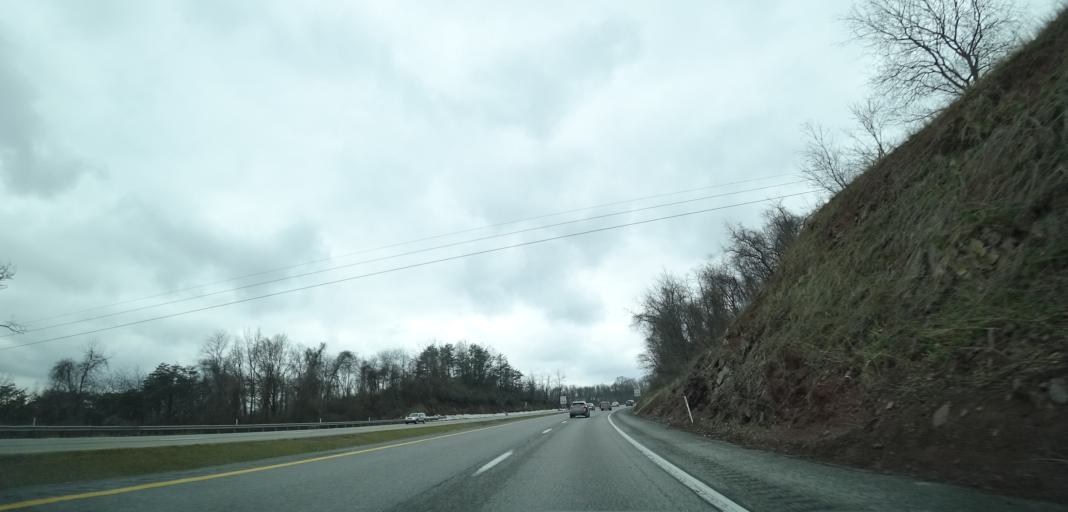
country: US
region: Pennsylvania
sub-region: Bedford County
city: Earlston
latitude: 39.9560
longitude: -78.2445
